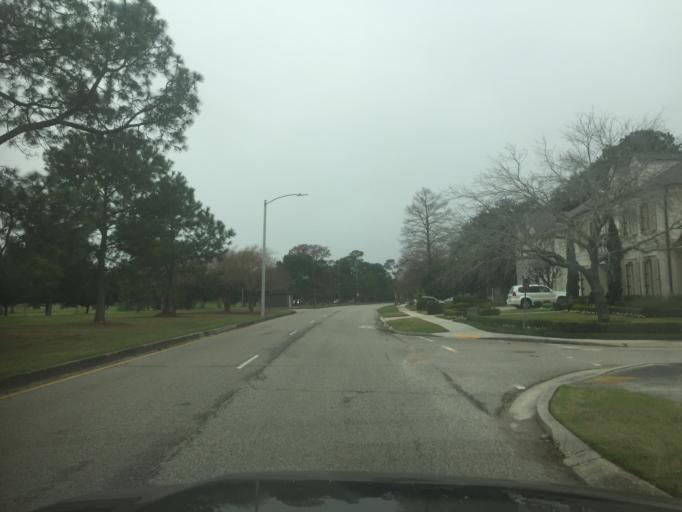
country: US
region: Louisiana
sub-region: Orleans Parish
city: New Orleans
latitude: 30.0187
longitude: -90.0909
